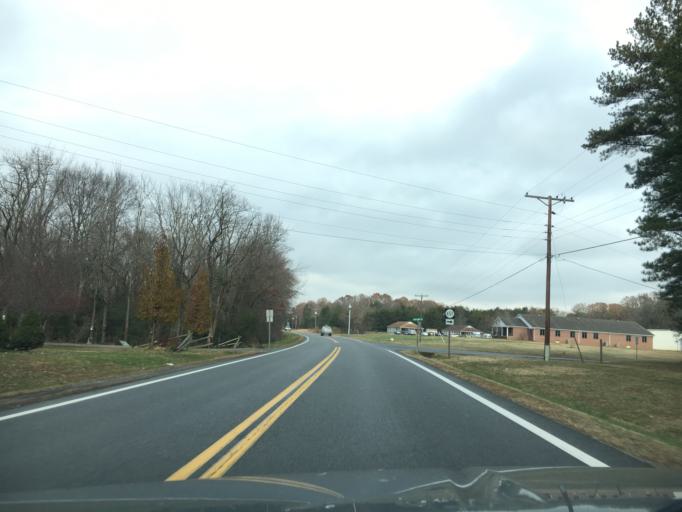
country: US
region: Virginia
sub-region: Prince Edward County
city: Farmville
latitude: 37.3490
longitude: -78.3824
